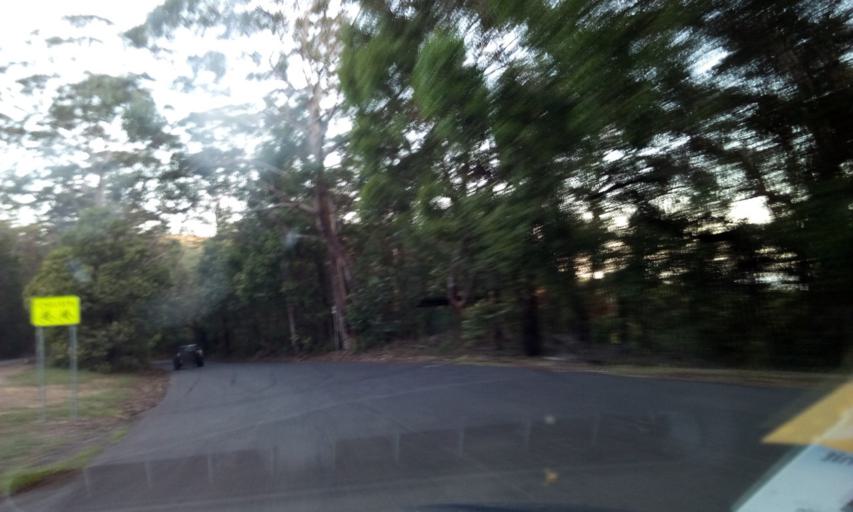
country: AU
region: New South Wales
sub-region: Wollongong
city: Mount Keira
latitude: -34.3956
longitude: 150.8502
